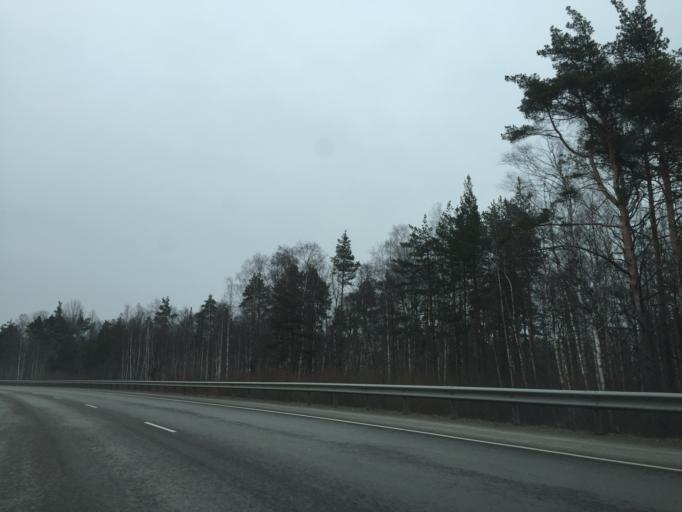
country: EE
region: Paernumaa
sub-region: Paernu linn
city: Parnu
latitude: 58.3850
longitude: 24.5570
